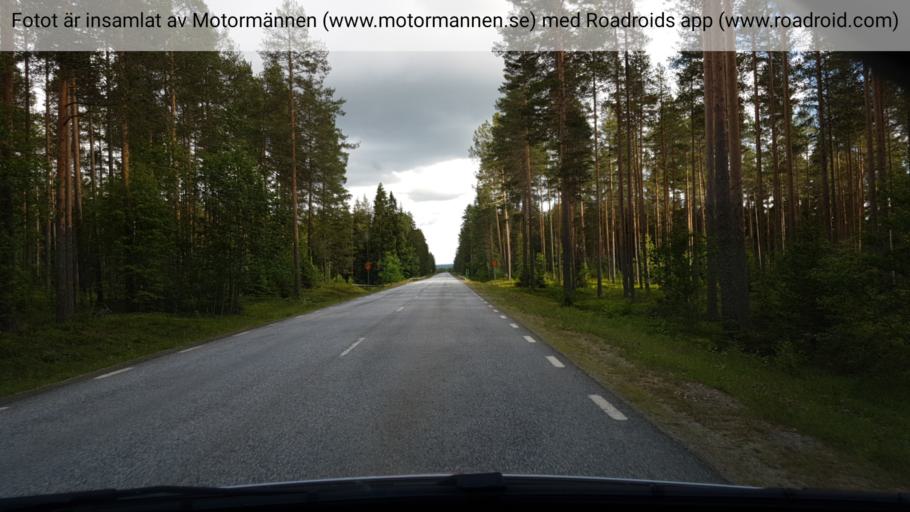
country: SE
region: Vaesterbotten
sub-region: Vindelns Kommun
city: Vindeln
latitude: 64.2144
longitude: 19.3931
